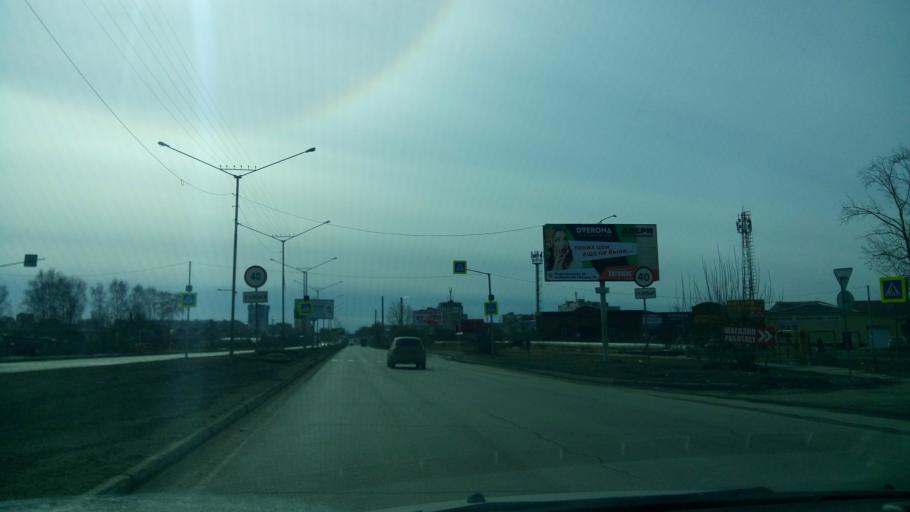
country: RU
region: Sverdlovsk
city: Nizhniy Tagil
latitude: 57.8939
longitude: 59.9409
